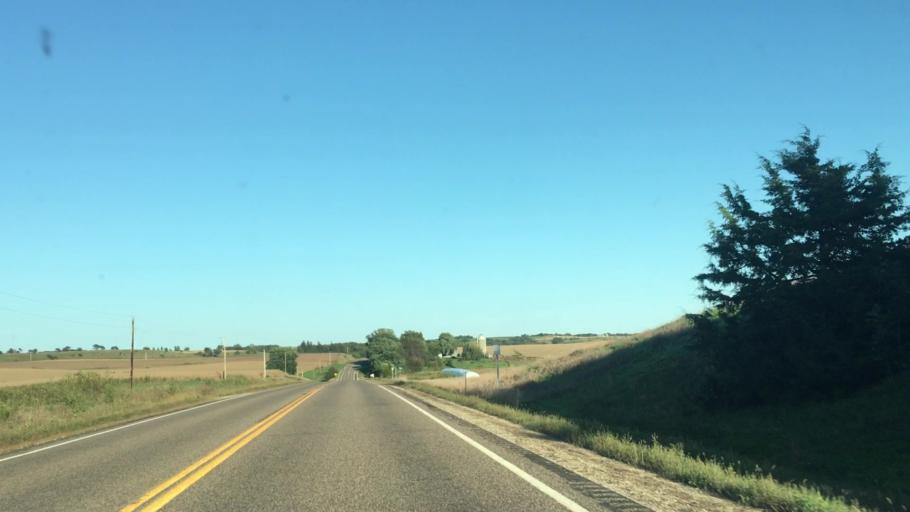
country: US
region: Minnesota
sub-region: Fillmore County
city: Chatfield
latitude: 43.8543
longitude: -92.1311
